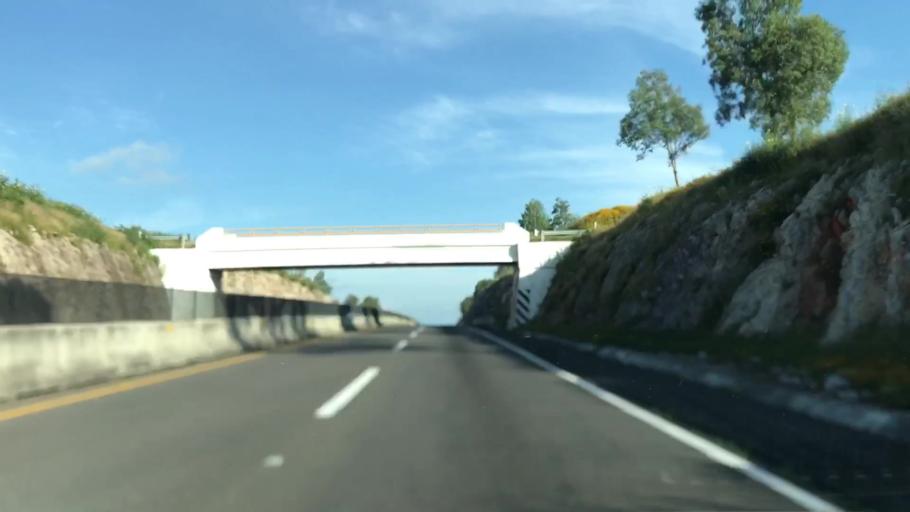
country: MX
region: Jalisco
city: Encarnacion de Diaz
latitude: 21.3837
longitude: -102.1406
